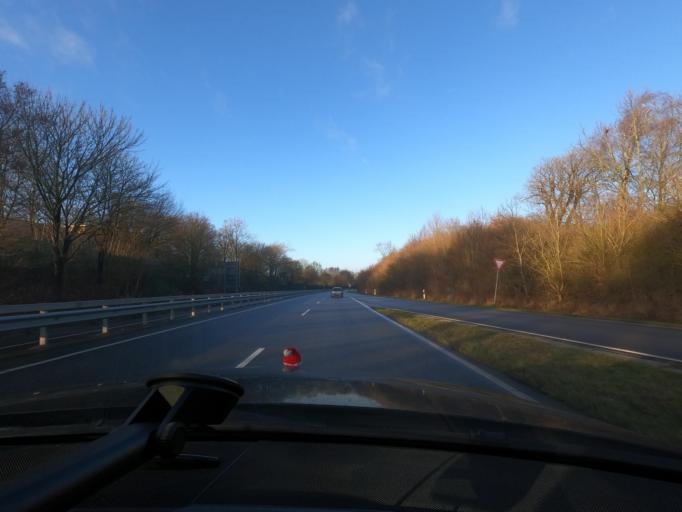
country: DE
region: Schleswig-Holstein
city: Harrislee
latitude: 54.8019
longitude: 9.4070
